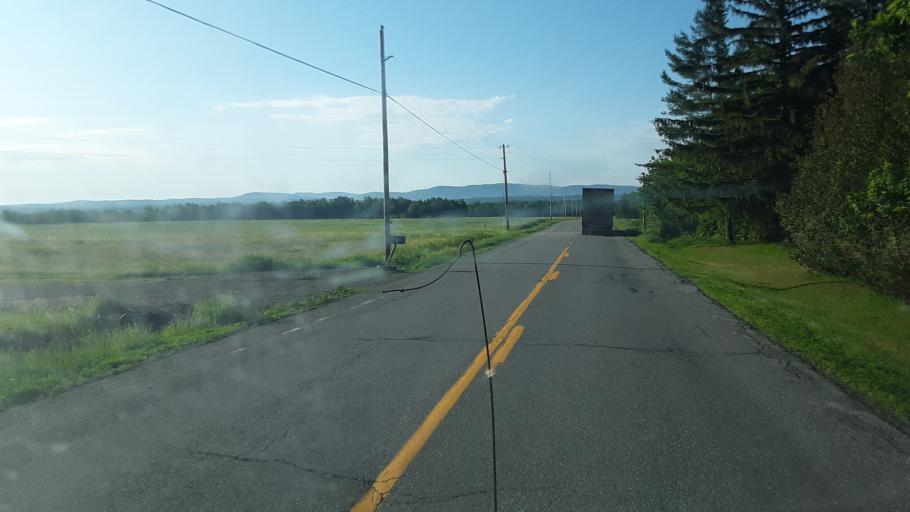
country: US
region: Maine
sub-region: Penobscot County
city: Patten
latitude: 46.1703
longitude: -68.2366
